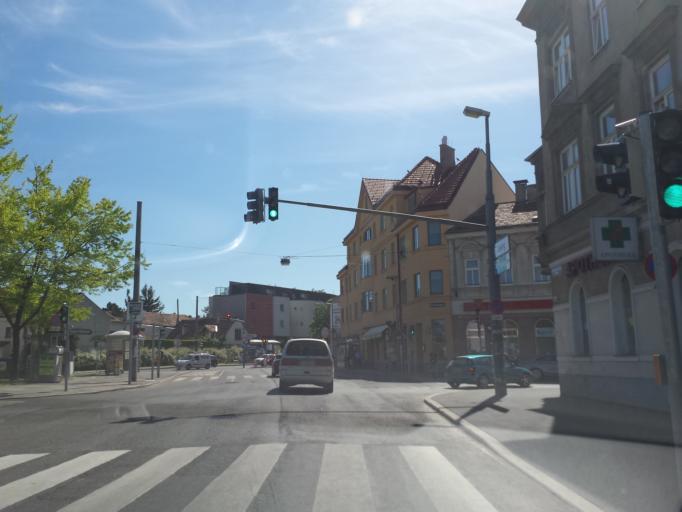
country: AT
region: Lower Austria
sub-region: Politischer Bezirk Modling
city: Perchtoldsdorf
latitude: 48.1464
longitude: 16.2962
